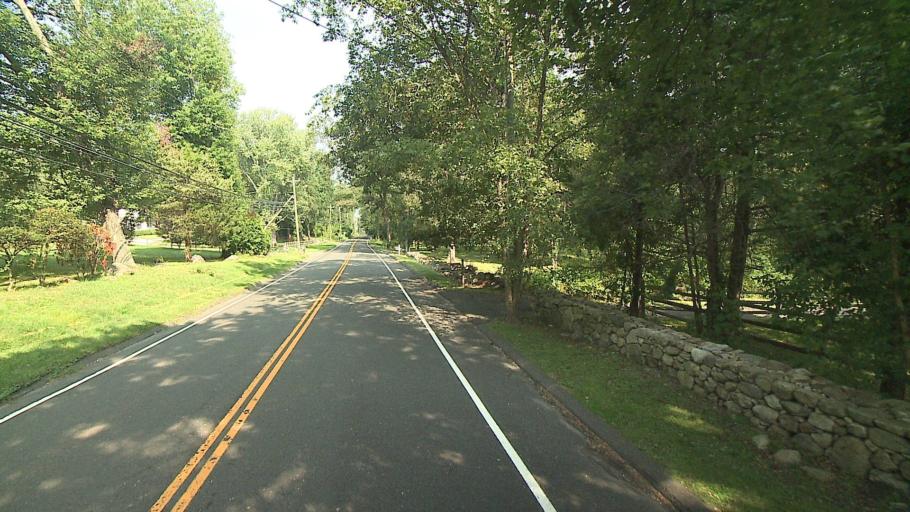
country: US
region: Connecticut
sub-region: Fairfield County
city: Georgetown
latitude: 41.2344
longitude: -73.4054
